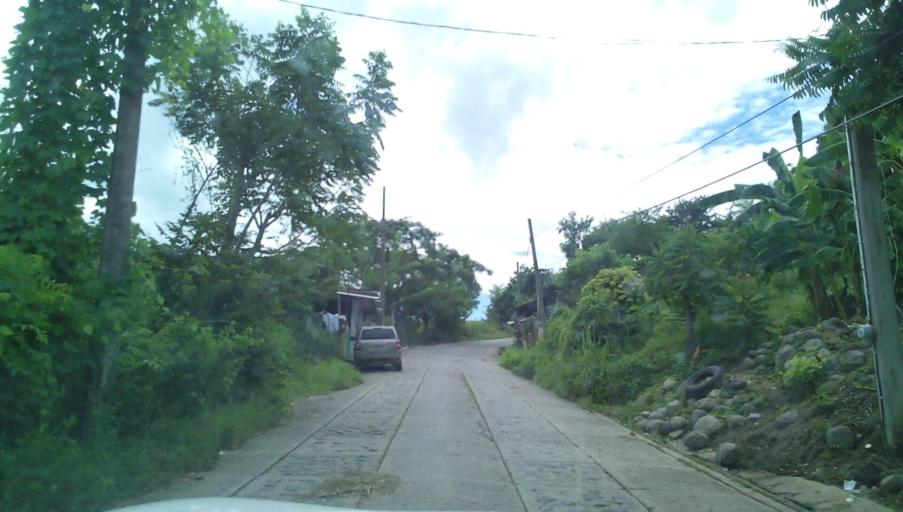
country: MX
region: Veracruz
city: Tepetzintla
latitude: 21.1598
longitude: -97.8521
